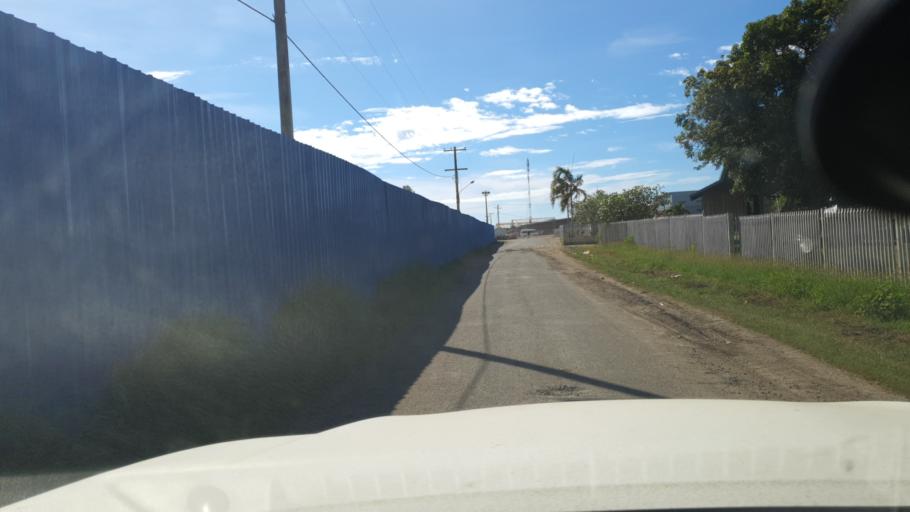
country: SB
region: Guadalcanal
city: Honiara
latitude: -9.4276
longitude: 160.0158
